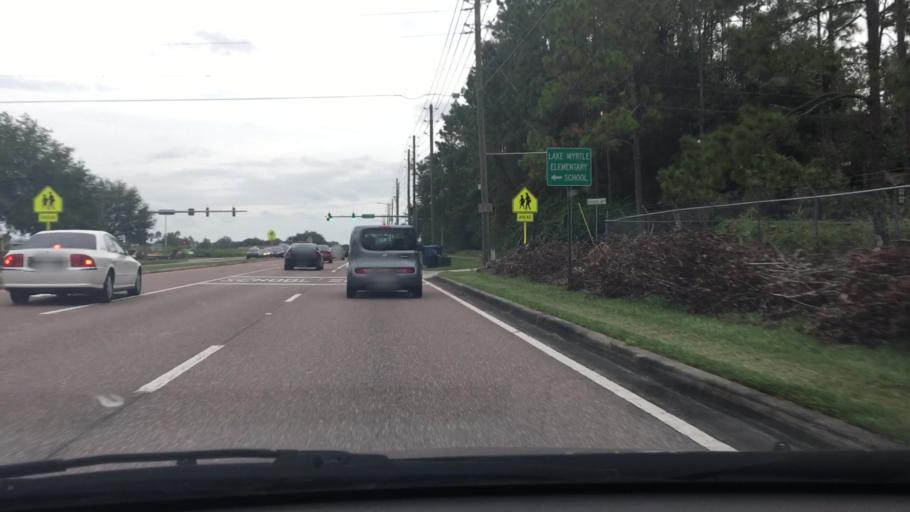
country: US
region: Florida
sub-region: Pasco County
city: Land O' Lakes
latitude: 28.1965
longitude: -82.4342
